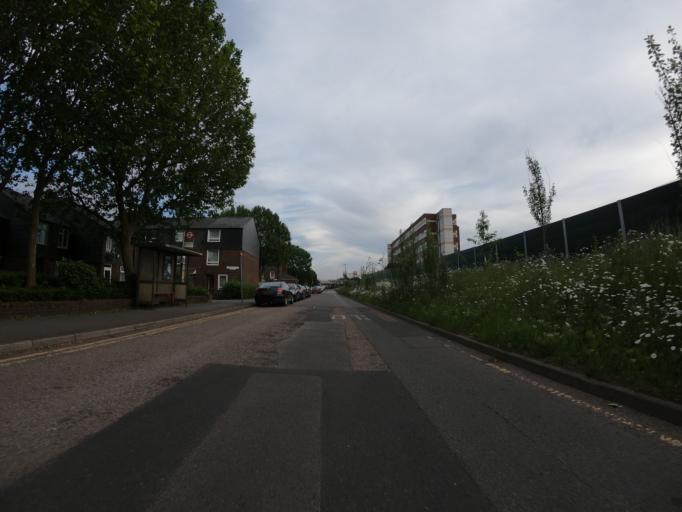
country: GB
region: England
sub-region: Greater London
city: Hackney
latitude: 51.5866
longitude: -0.0598
